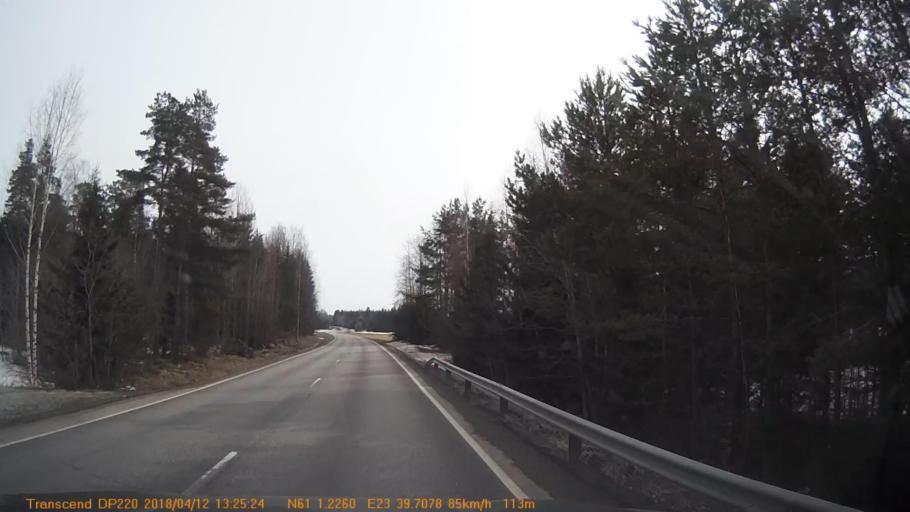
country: FI
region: Pirkanmaa
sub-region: Etelae-Pirkanmaa
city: Kylmaekoski
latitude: 61.0202
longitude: 23.6621
